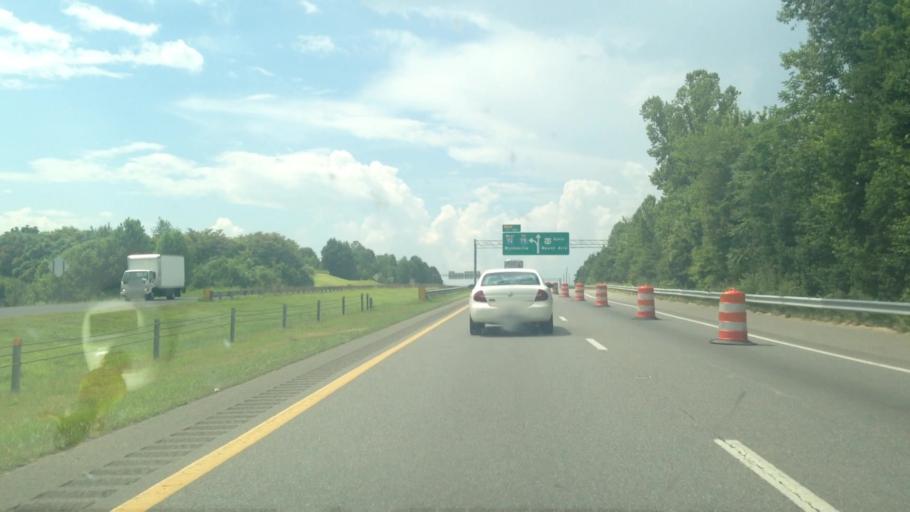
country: US
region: North Carolina
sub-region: Surry County
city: Flat Rock
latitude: 36.4424
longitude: -80.5403
